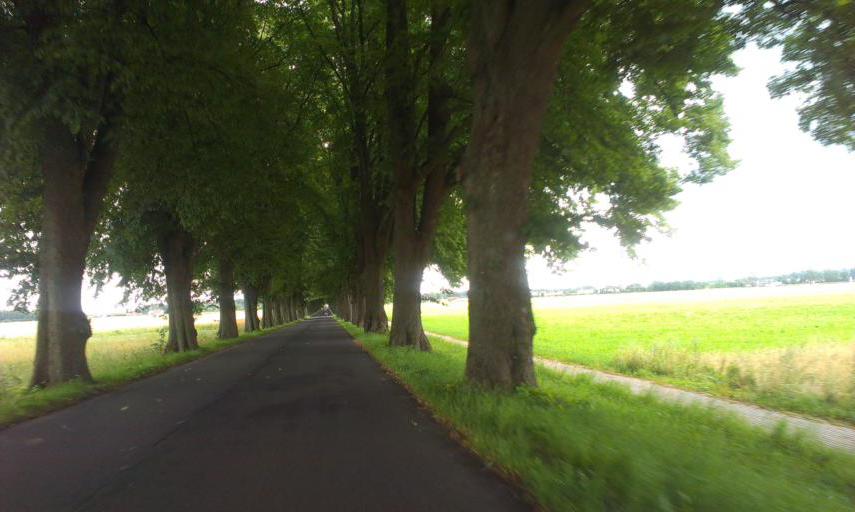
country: PL
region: West Pomeranian Voivodeship
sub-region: Powiat bialogardzki
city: Tychowo
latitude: 53.9350
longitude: 16.2432
